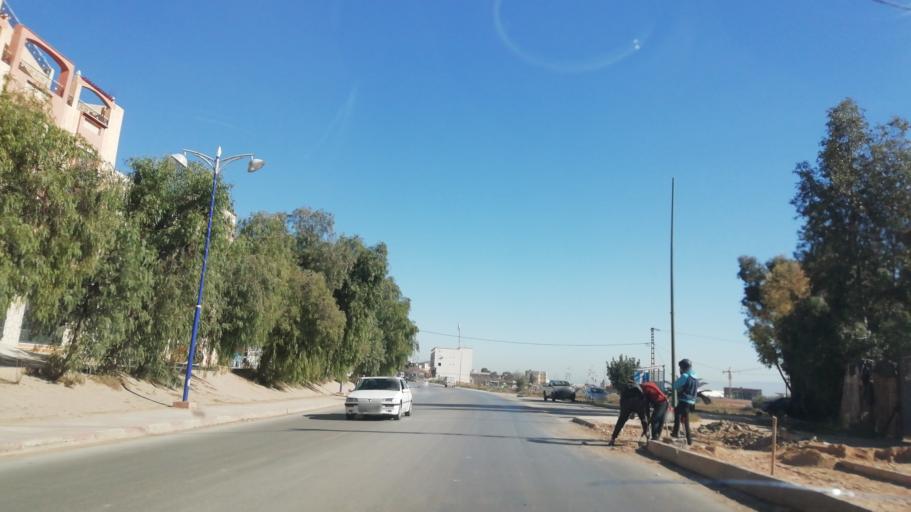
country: DZ
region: Tlemcen
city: Nedroma
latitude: 34.8419
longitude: -1.7637
